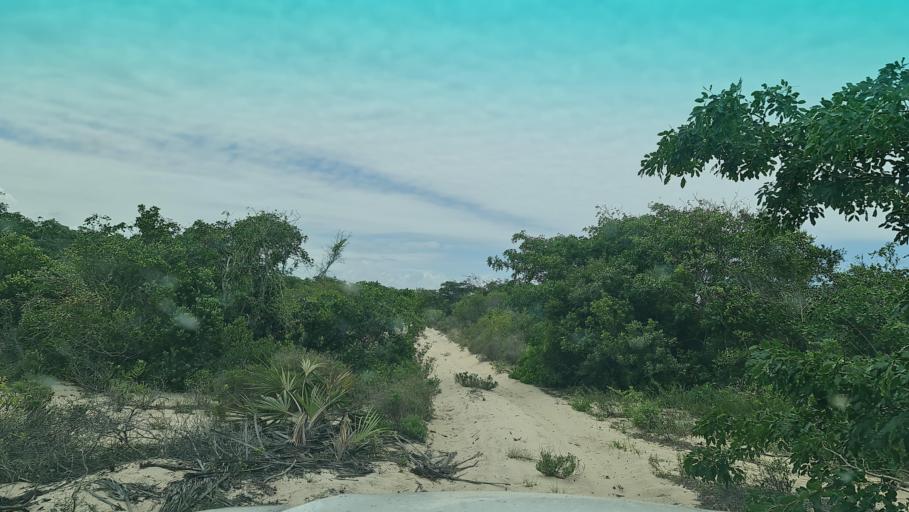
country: MZ
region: Maputo
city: Manhica
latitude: -25.6330
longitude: 32.7866
